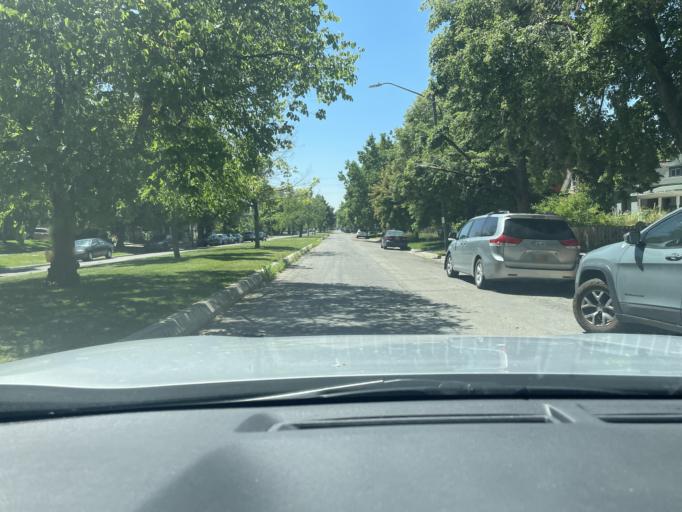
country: US
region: Utah
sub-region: Salt Lake County
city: Salt Lake City
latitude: 40.7555
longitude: -111.8740
